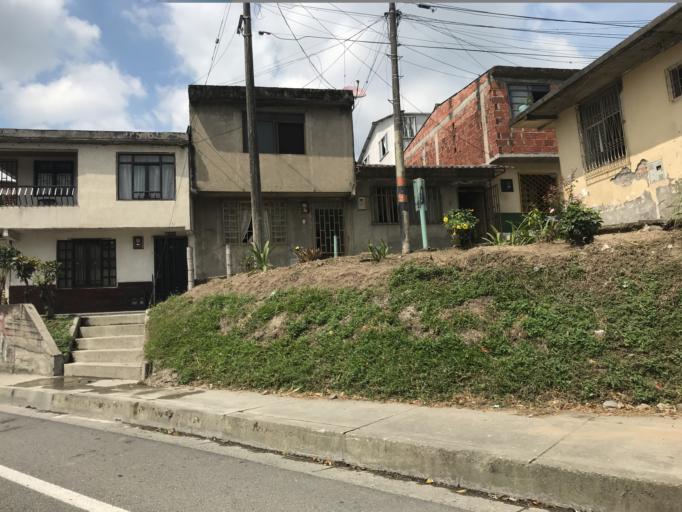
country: CO
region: Quindio
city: Calarca
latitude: 4.5193
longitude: -75.6487
